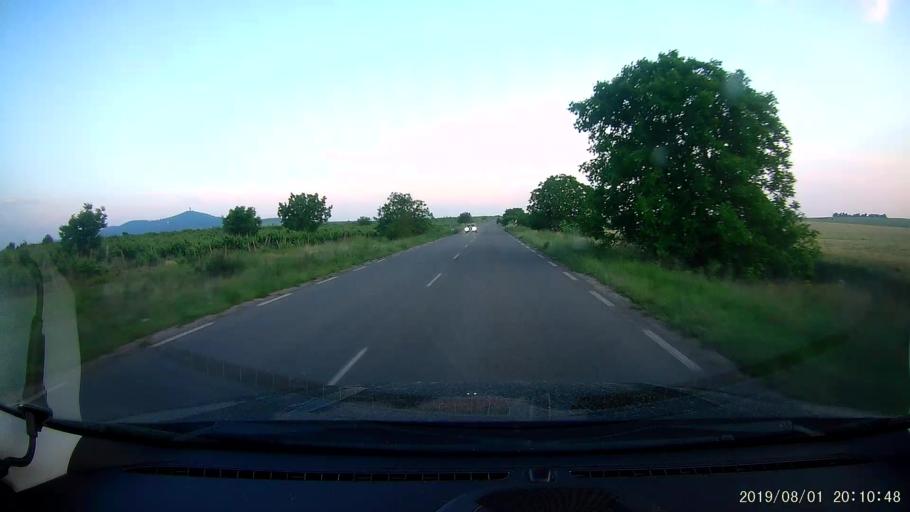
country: BG
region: Yambol
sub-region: Obshtina Yambol
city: Yambol
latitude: 42.4742
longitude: 26.6028
